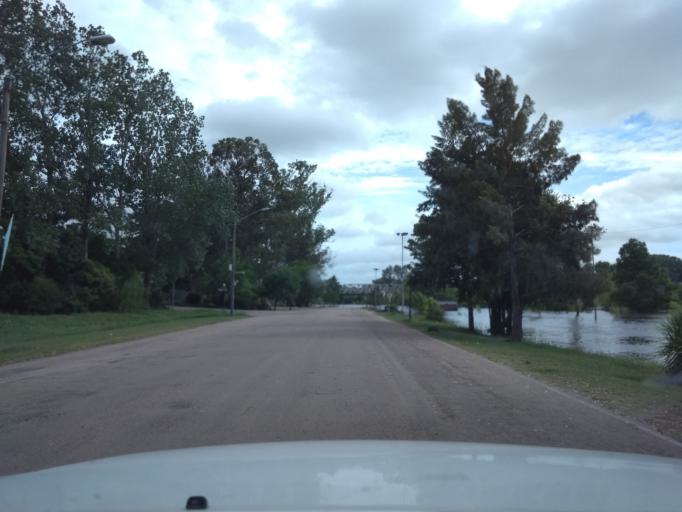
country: UY
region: Florida
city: Florida
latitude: -34.1024
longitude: -56.2036
